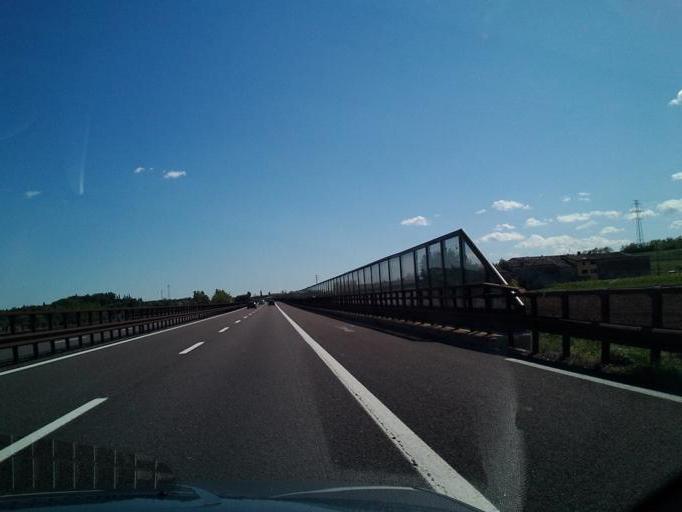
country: IT
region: Veneto
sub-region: Provincia di Verona
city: Pastrengo
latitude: 45.5080
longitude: 10.7843
